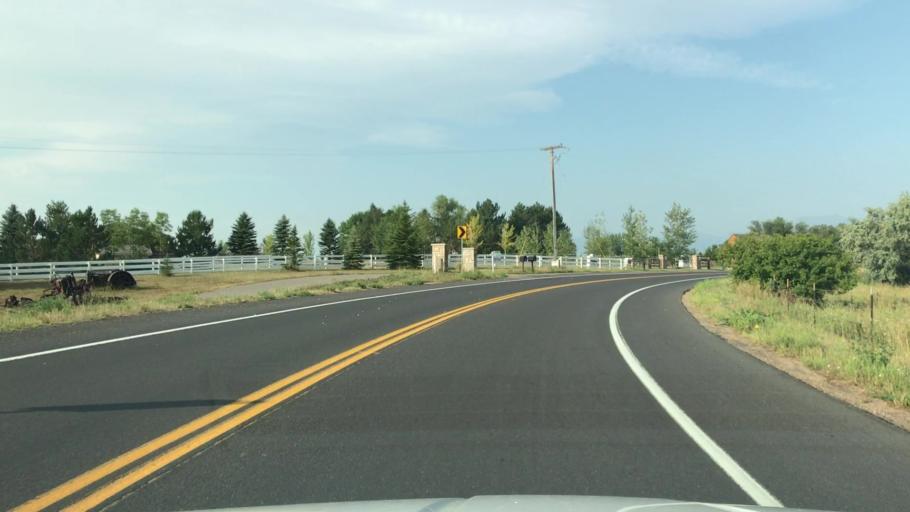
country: US
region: Colorado
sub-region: Boulder County
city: Gunbarrel
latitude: 40.0370
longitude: -105.1551
